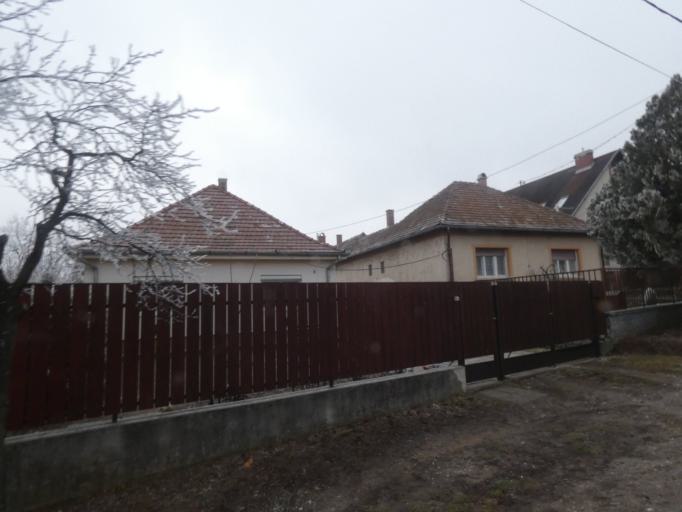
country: HU
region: Pest
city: Szada
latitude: 47.6316
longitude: 19.3057
